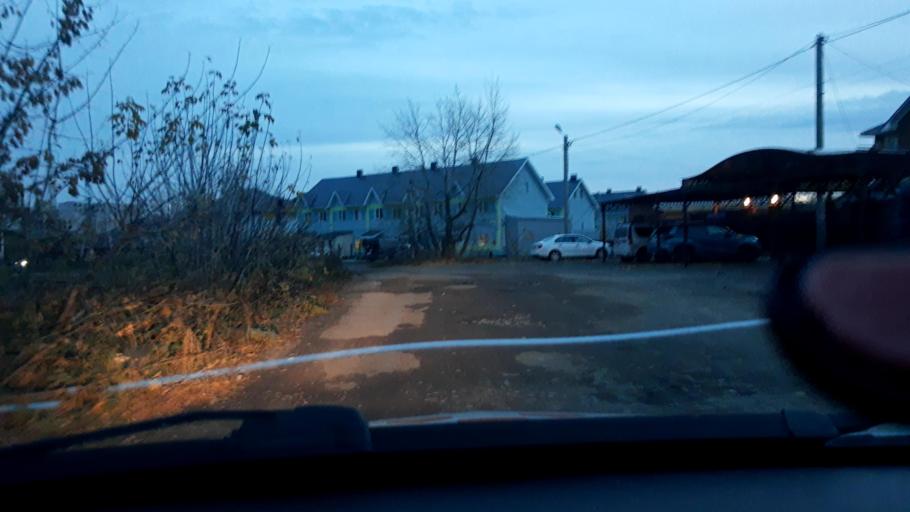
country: RU
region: Bashkortostan
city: Ufa
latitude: 54.6872
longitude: 55.9783
